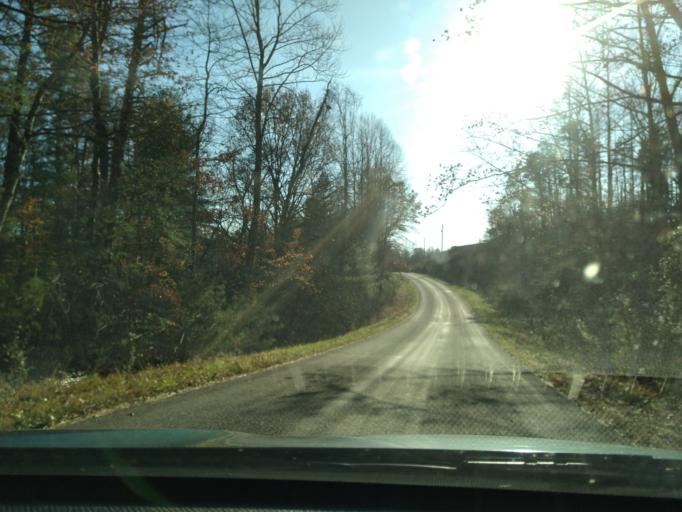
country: US
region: Virginia
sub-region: Floyd County
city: Floyd
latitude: 36.8255
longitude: -80.2114
